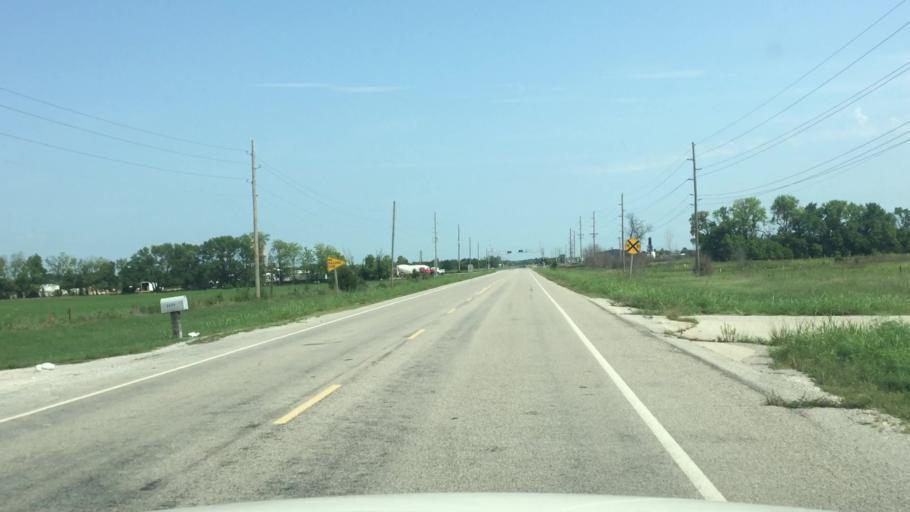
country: US
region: Kansas
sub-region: Montgomery County
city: Coffeyville
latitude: 37.0839
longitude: -95.5863
